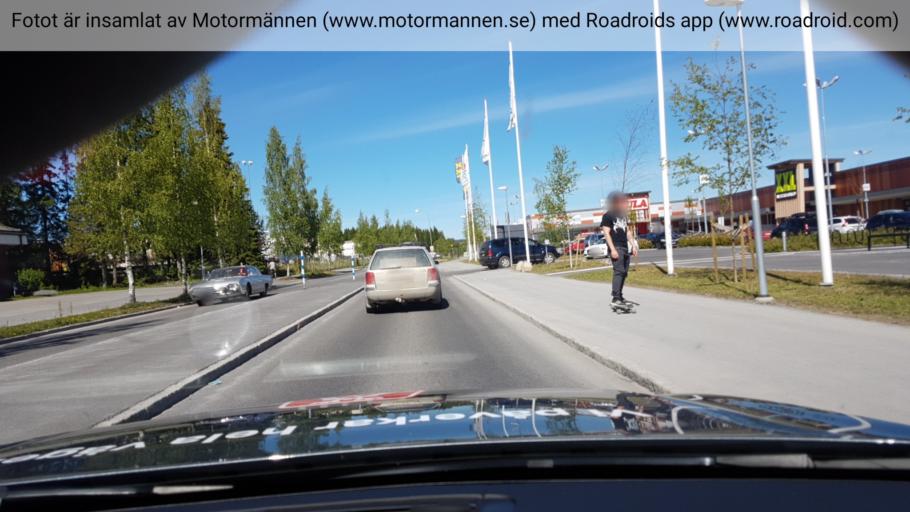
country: SE
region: Jaemtland
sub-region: OEstersunds Kommun
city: Ostersund
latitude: 63.1720
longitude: 14.6902
